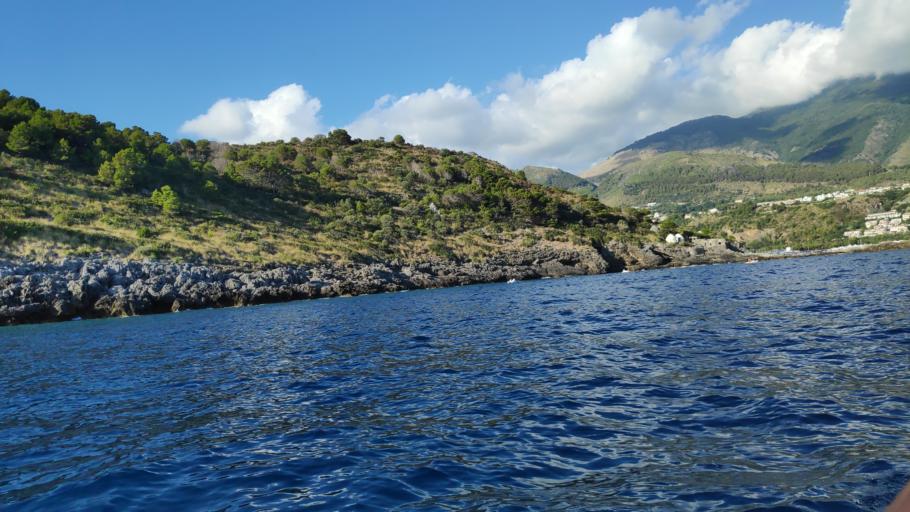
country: IT
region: Calabria
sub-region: Provincia di Cosenza
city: Praia a Mare
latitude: 39.8710
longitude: 15.7756
